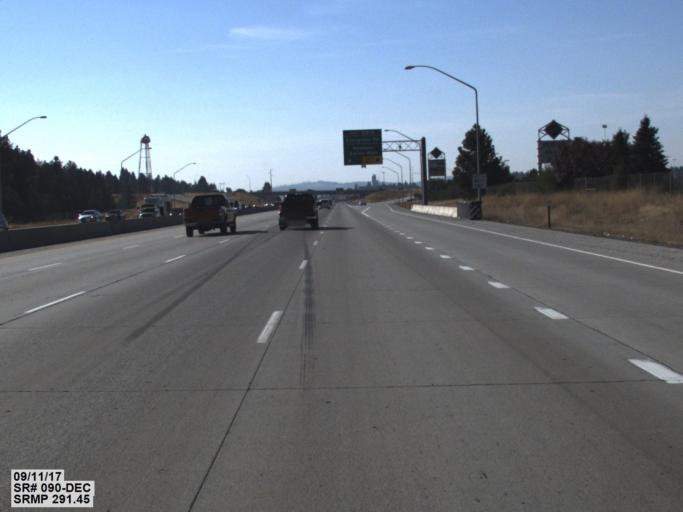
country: US
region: Washington
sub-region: Spokane County
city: Veradale
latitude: 47.6712
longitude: -117.2060
